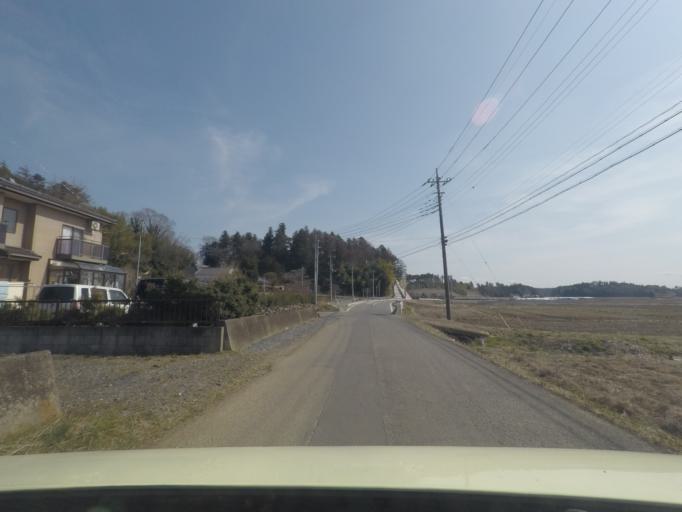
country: JP
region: Ibaraki
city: Ishioka
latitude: 36.1950
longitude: 140.3379
